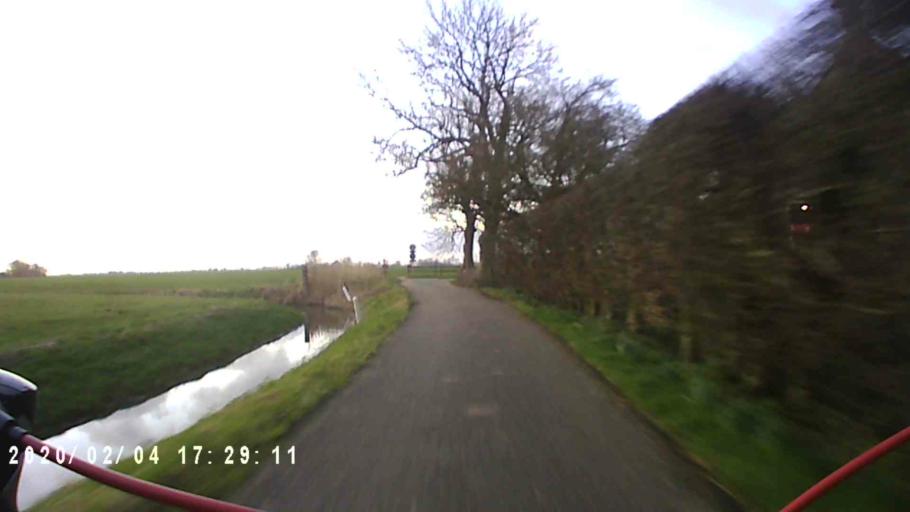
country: NL
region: Groningen
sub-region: Gemeente Zuidhorn
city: Aduard
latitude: 53.2719
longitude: 6.5047
